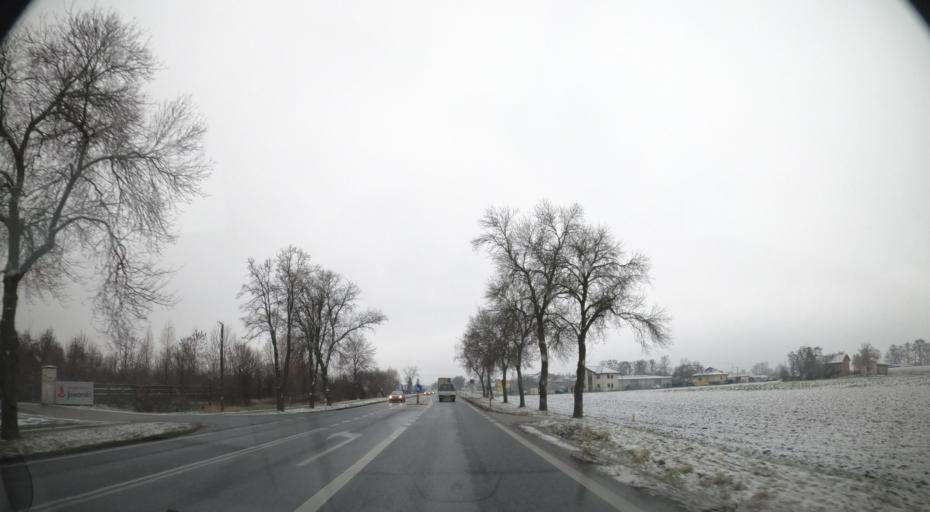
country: PL
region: Masovian Voivodeship
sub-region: Powiat warszawski zachodni
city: Bieniewice
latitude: 52.2037
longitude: 20.5193
